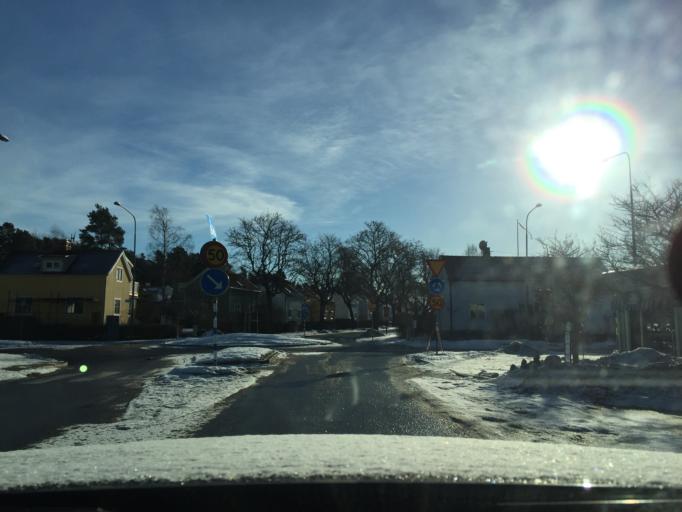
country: SE
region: Stockholm
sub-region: Stockholms Kommun
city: Bromma
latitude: 59.3515
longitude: 17.9001
